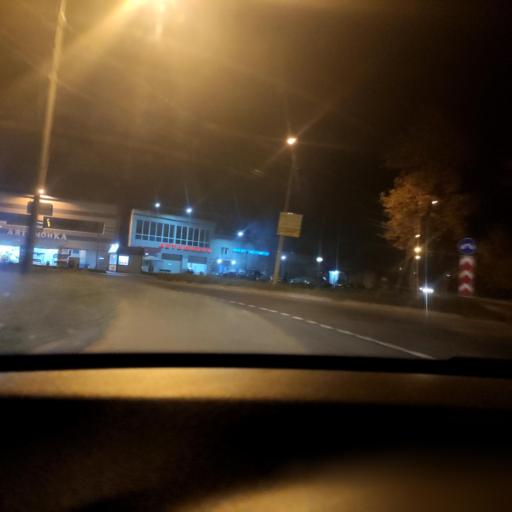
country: RU
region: Samara
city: Smyshlyayevka
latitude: 53.2324
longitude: 50.3080
